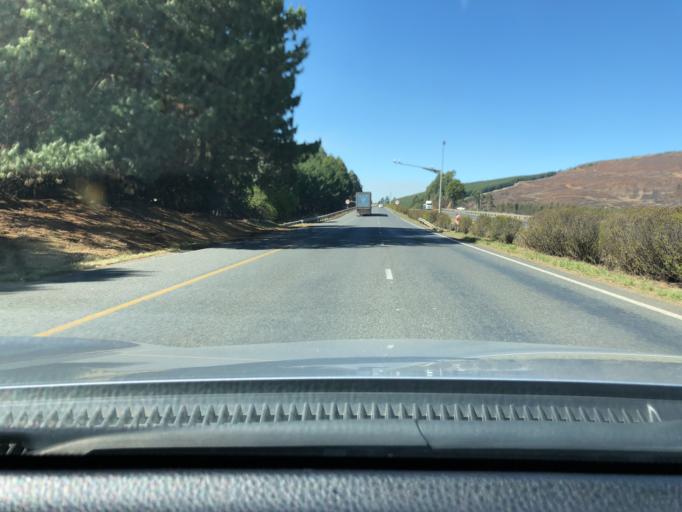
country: ZA
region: KwaZulu-Natal
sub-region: uMgungundlovu District Municipality
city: Howick
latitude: -29.3617
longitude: 30.1007
